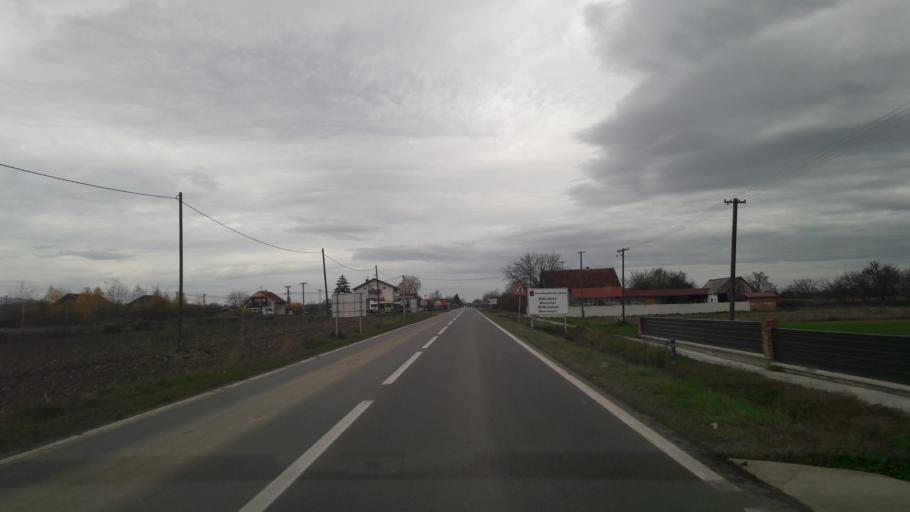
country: HR
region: Osjecko-Baranjska
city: Fericanci
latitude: 45.5314
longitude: 17.9483
